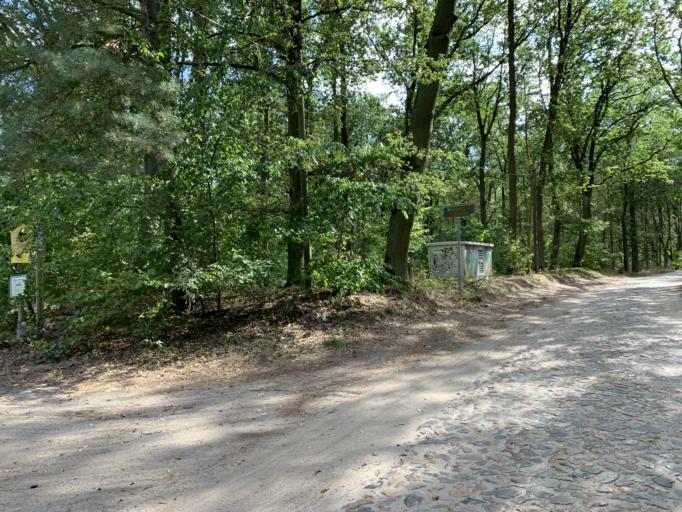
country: DE
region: Brandenburg
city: Michendorf
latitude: 52.3108
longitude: 12.9739
